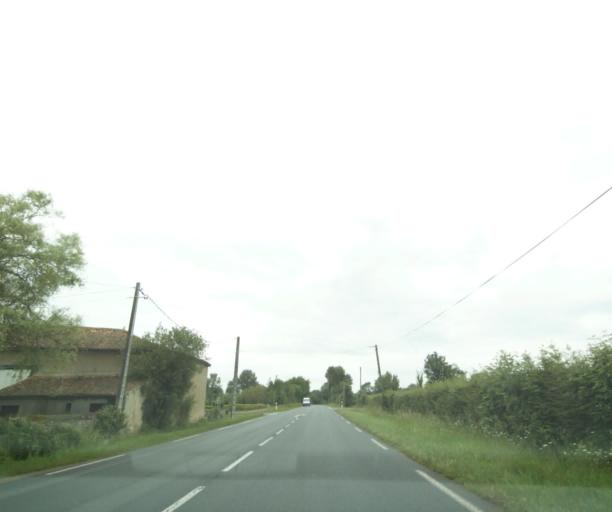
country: FR
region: Poitou-Charentes
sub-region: Departement des Deux-Sevres
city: Viennay
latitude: 46.7073
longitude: -0.2392
